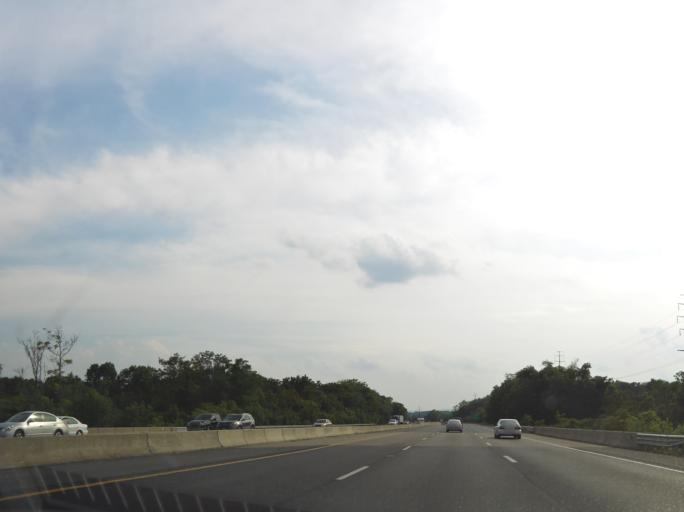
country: US
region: Maryland
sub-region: Washington County
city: Williamsport
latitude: 39.5629
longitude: -77.8977
